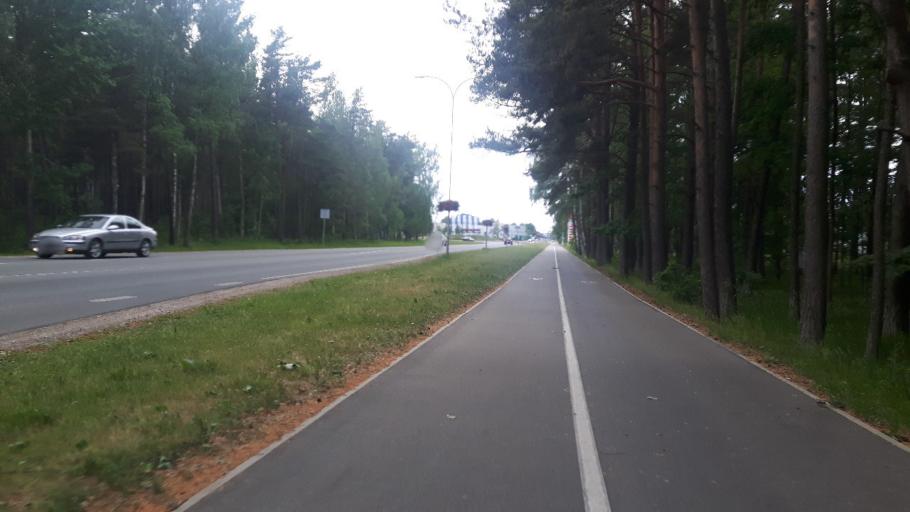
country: LV
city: Tireli
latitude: 56.9596
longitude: 23.6242
